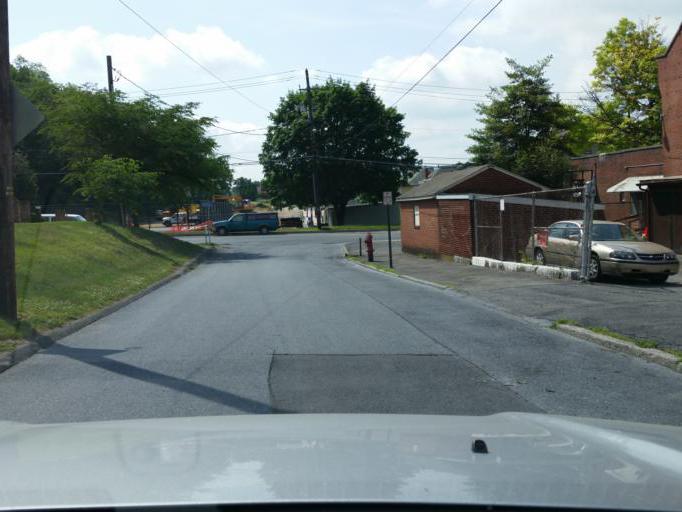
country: US
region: Pennsylvania
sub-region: Dauphin County
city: Enhaut
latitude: 40.2307
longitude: -76.8322
